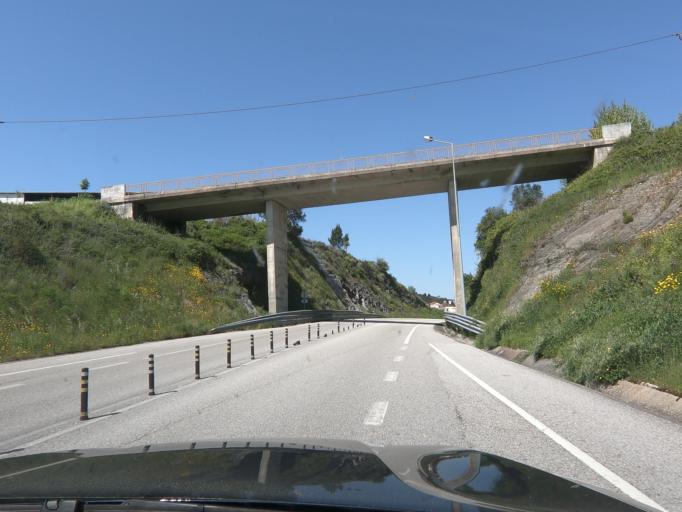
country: PT
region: Coimbra
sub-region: Vila Nova de Poiares
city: Poiares
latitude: 40.1772
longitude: -8.2671
